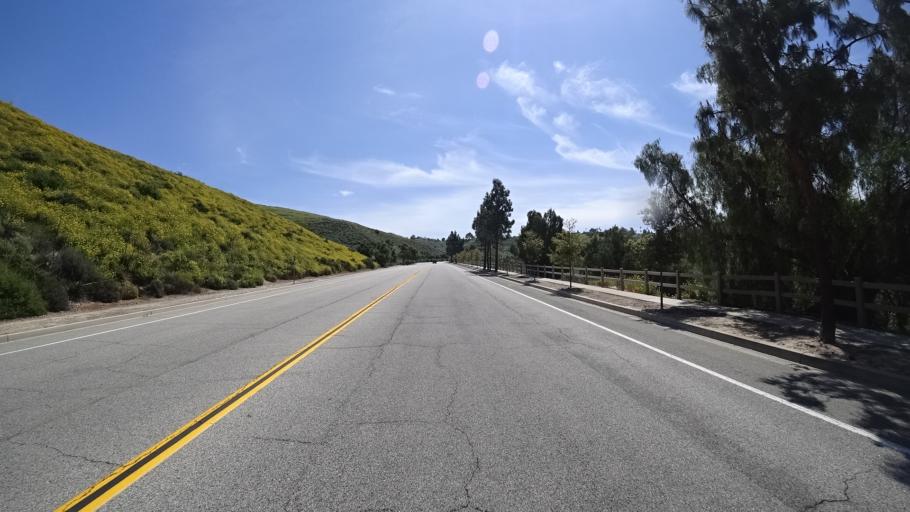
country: US
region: California
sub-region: Ventura County
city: Thousand Oaks
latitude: 34.2333
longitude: -118.8404
